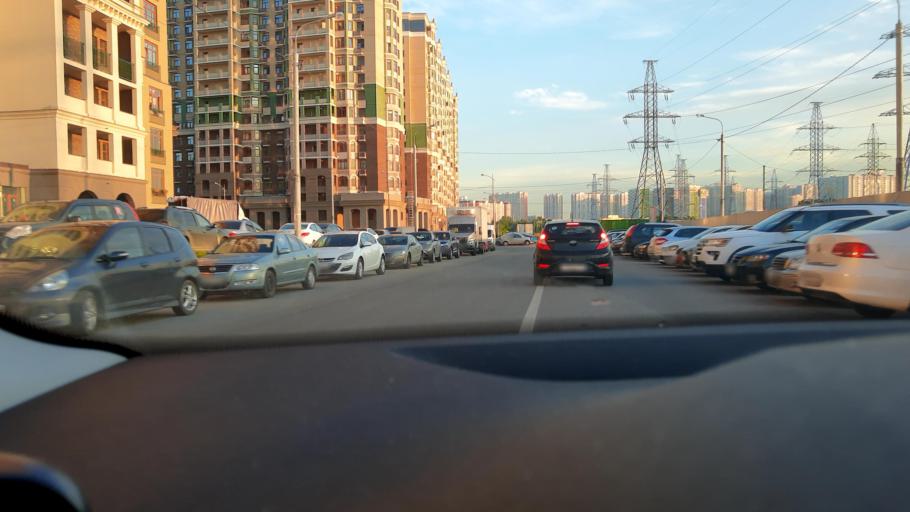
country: RU
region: Moscow
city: Khimki
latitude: 55.9181
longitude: 37.4083
